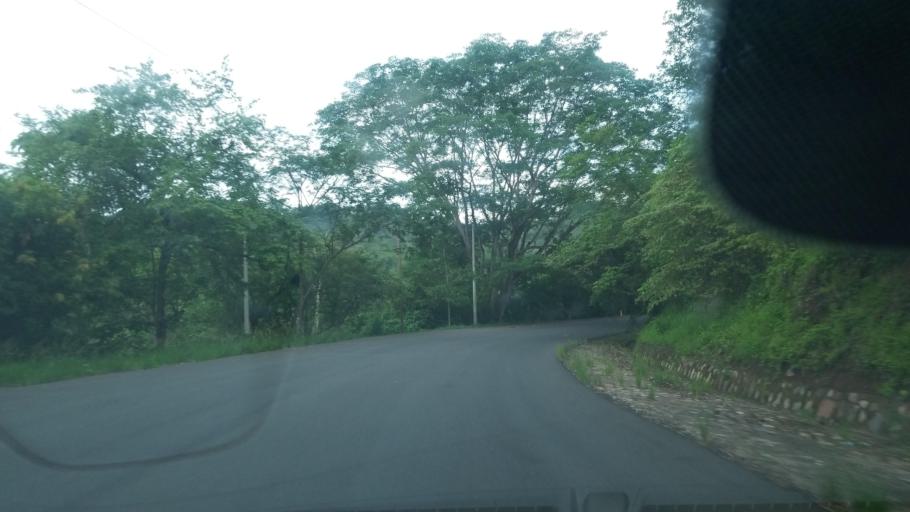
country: HN
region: Santa Barbara
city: Concepcion del Sur
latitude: 14.8159
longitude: -88.1780
